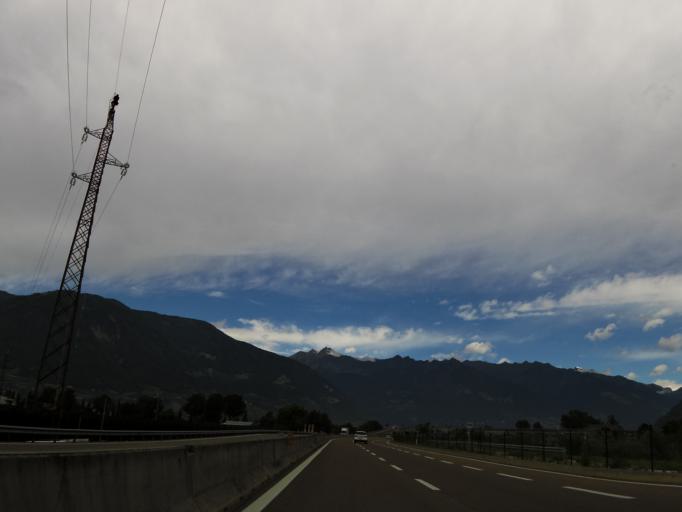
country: IT
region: Trentino-Alto Adige
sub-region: Bolzano
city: Postal
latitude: 46.6062
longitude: 11.1821
